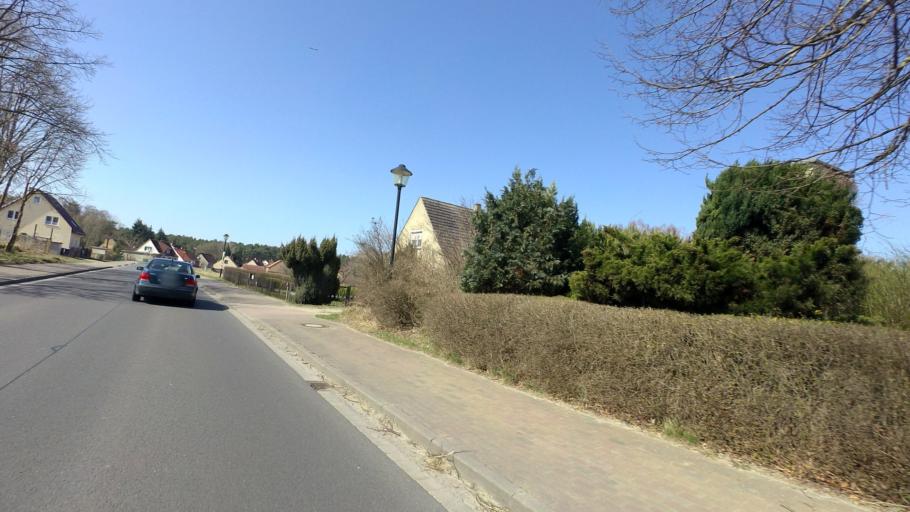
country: DE
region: Brandenburg
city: Ruthnick
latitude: 52.9063
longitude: 12.9642
